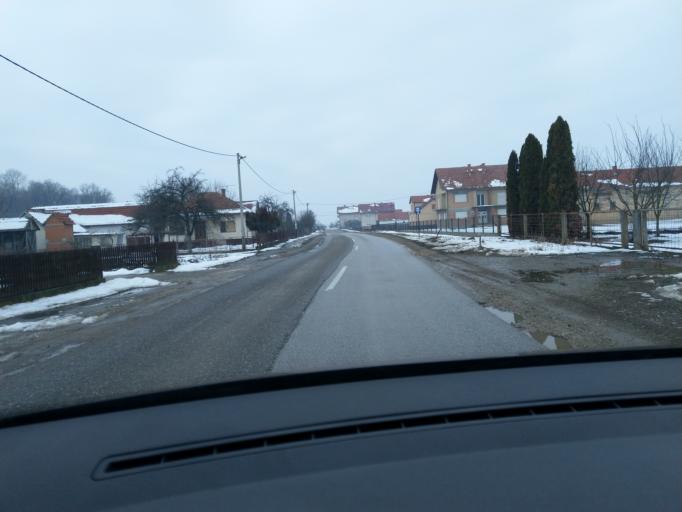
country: BA
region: Republika Srpska
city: Velika Obarska
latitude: 44.7861
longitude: 19.1869
